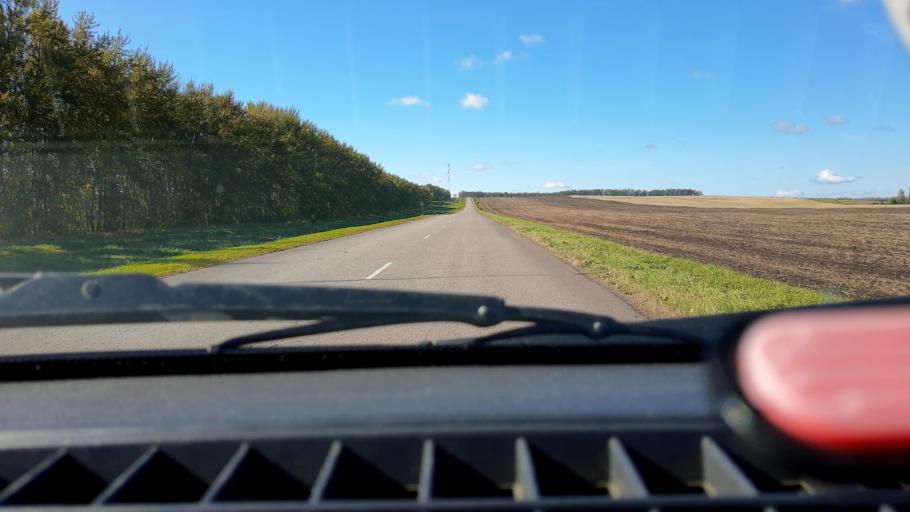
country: RU
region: Bashkortostan
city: Kushnarenkovo
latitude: 55.0836
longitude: 55.4760
